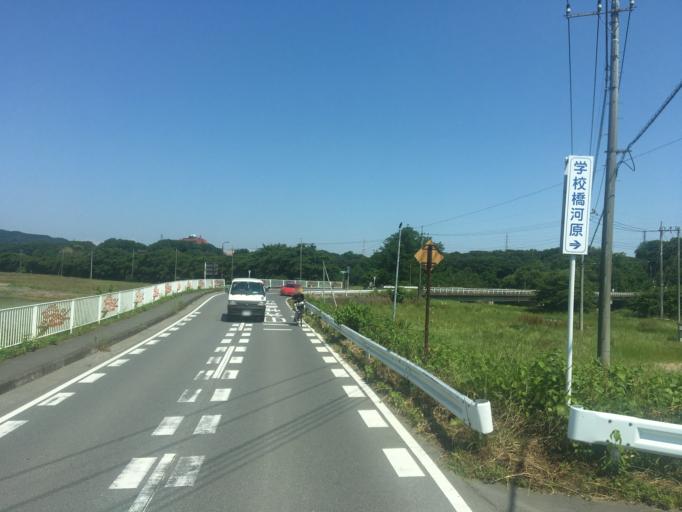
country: JP
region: Saitama
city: Ogawa
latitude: 36.0312
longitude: 139.3317
